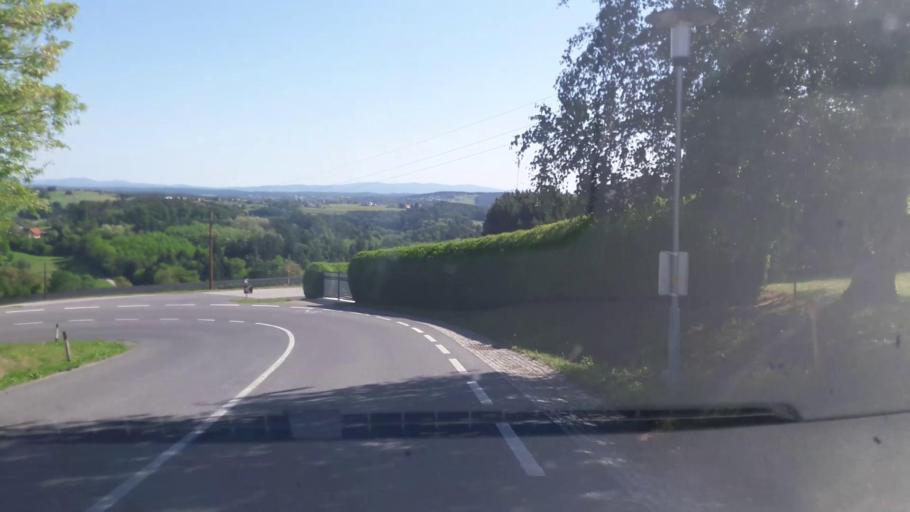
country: AT
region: Styria
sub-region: Politischer Bezirk Hartberg-Fuerstenfeld
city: Neudau
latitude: 47.1694
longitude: 16.1262
